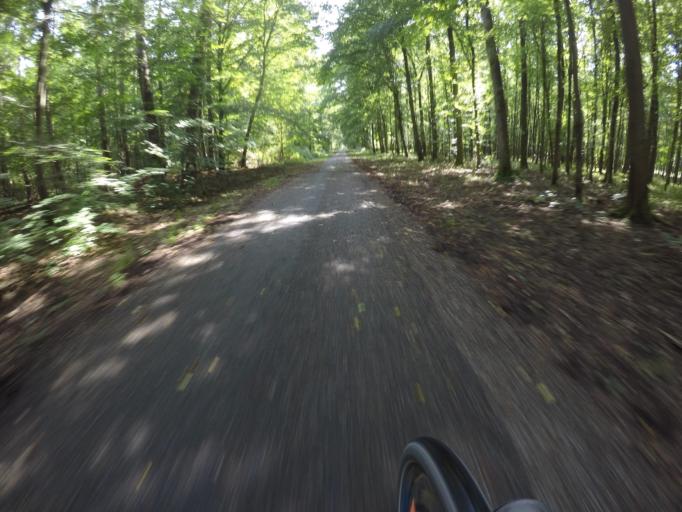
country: DE
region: Baden-Wuerttemberg
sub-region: Karlsruhe Region
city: Hambrucken
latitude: 49.2163
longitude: 8.5769
